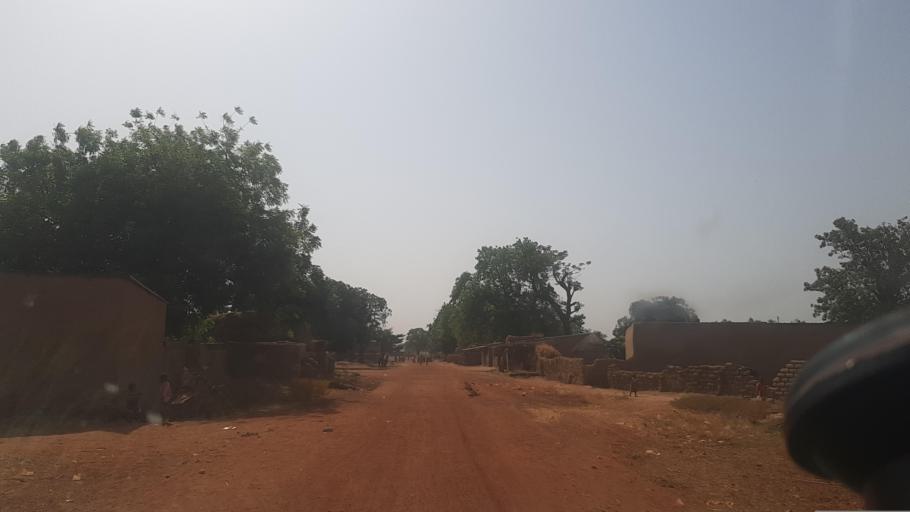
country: ML
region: Segou
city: Baroueli
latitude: 13.0126
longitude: -6.4227
